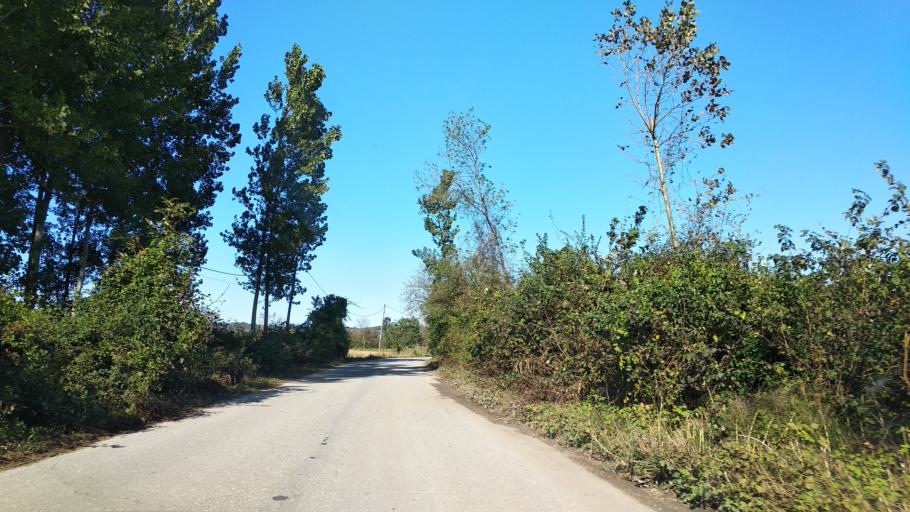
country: TR
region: Sakarya
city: Ortakoy
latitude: 41.0311
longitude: 30.6078
